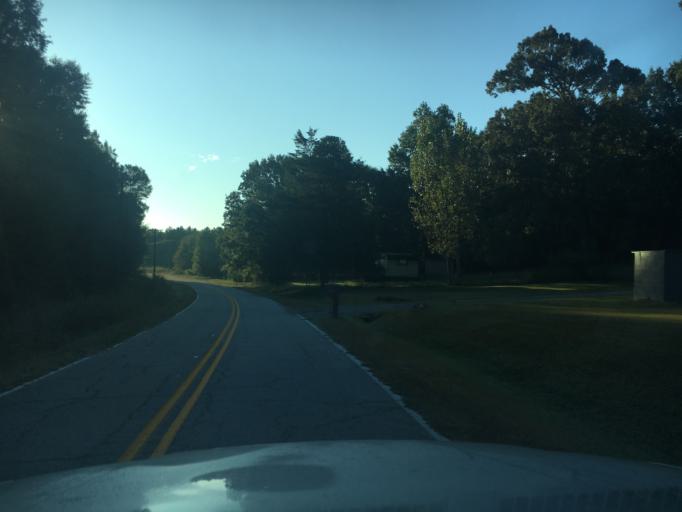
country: US
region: South Carolina
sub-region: Spartanburg County
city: Woodruff
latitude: 34.7878
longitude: -82.0031
